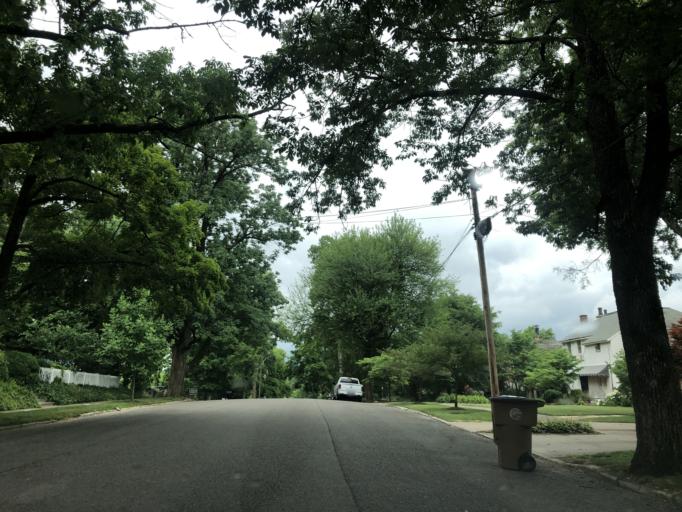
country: US
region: Tennessee
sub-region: Davidson County
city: Belle Meade
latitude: 36.1317
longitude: -86.8271
